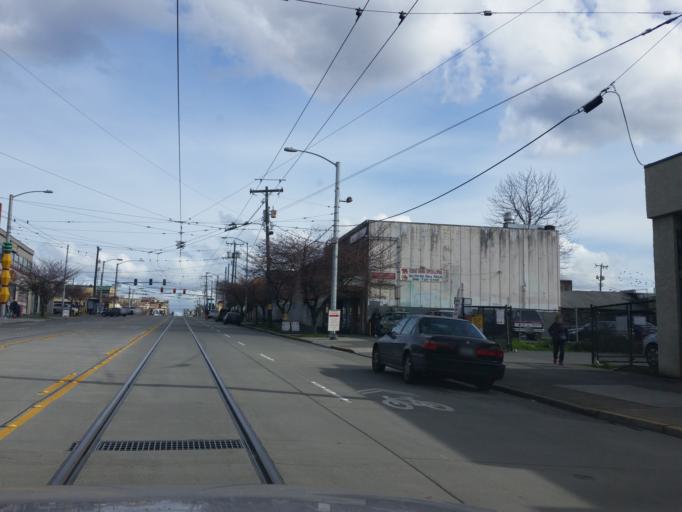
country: US
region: Washington
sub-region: King County
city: Seattle
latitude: 47.5992
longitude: -122.3196
